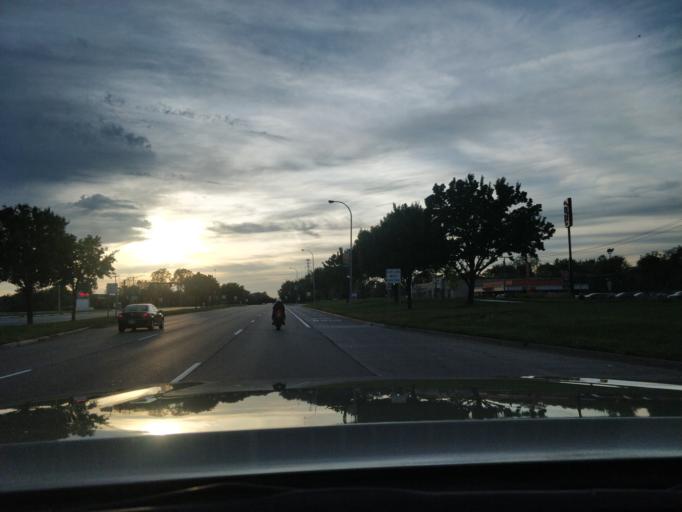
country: US
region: Michigan
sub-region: Wayne County
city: Southgate
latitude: 42.1983
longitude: -83.2411
